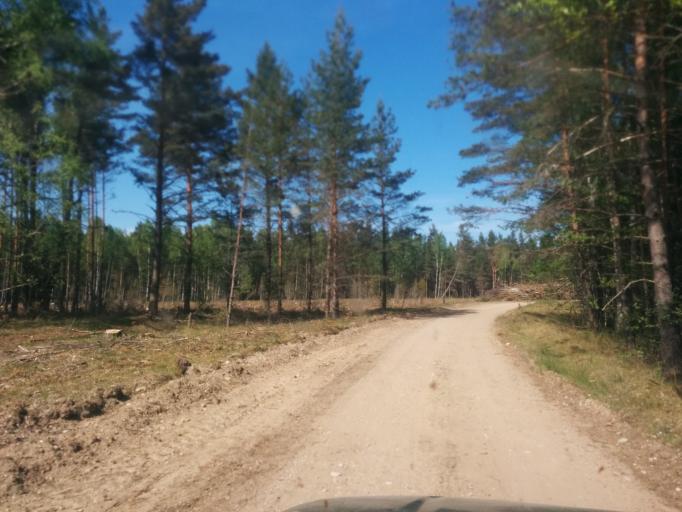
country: LV
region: Dundaga
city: Dundaga
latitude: 57.6194
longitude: 22.0895
